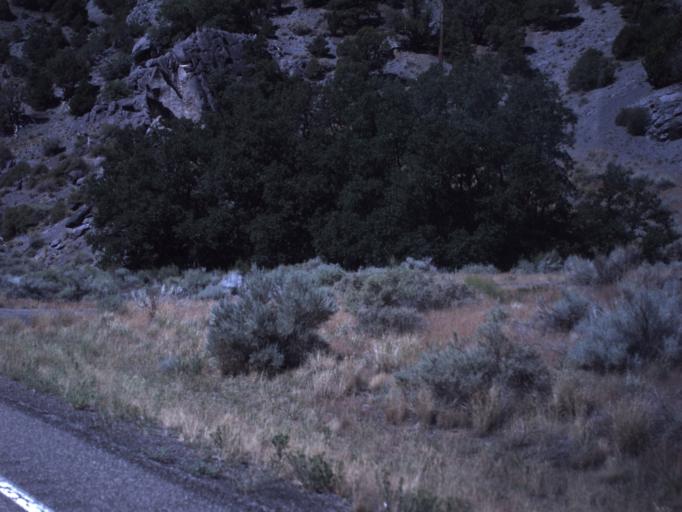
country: US
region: Utah
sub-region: Sevier County
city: Monroe
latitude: 38.5334
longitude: -112.2707
